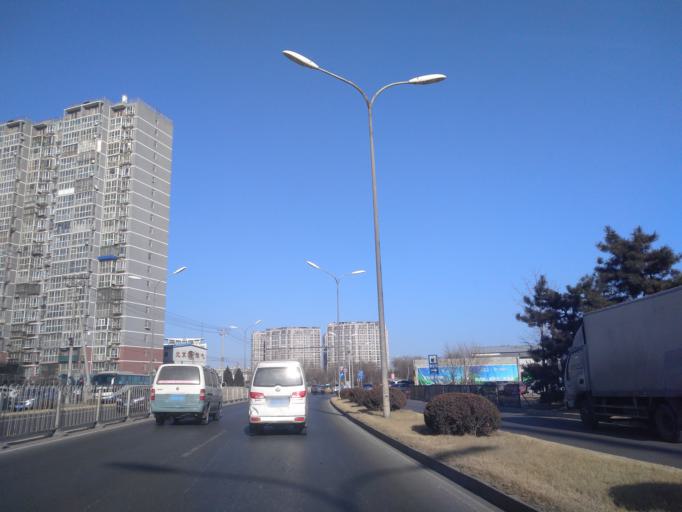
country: CN
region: Beijing
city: Jiugong
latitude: 39.8288
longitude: 116.4710
